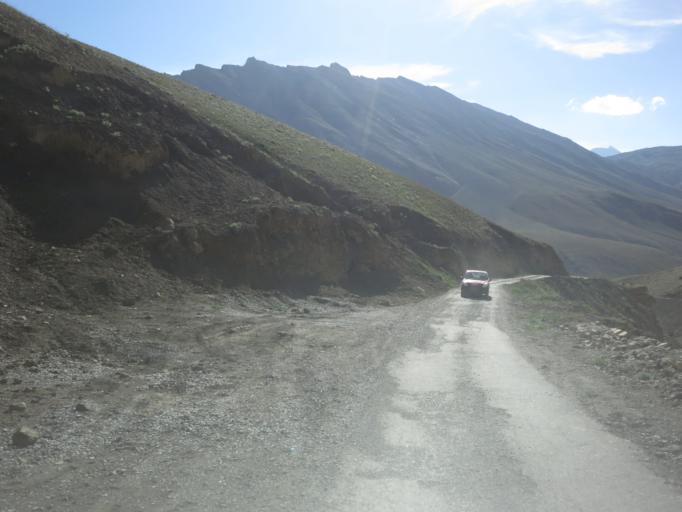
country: IN
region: Himachal Pradesh
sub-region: Kulu
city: Manali
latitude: 32.3246
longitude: 78.0090
